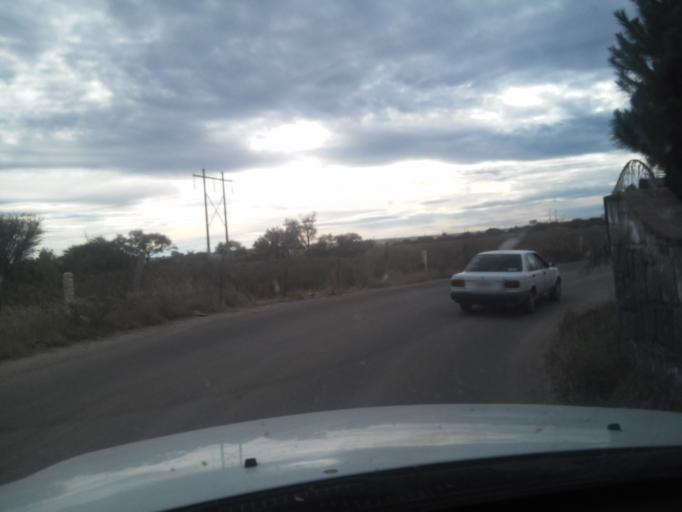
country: MX
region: Durango
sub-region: Durango
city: Jose Refugio Salcido
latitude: 24.0300
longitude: -104.5673
